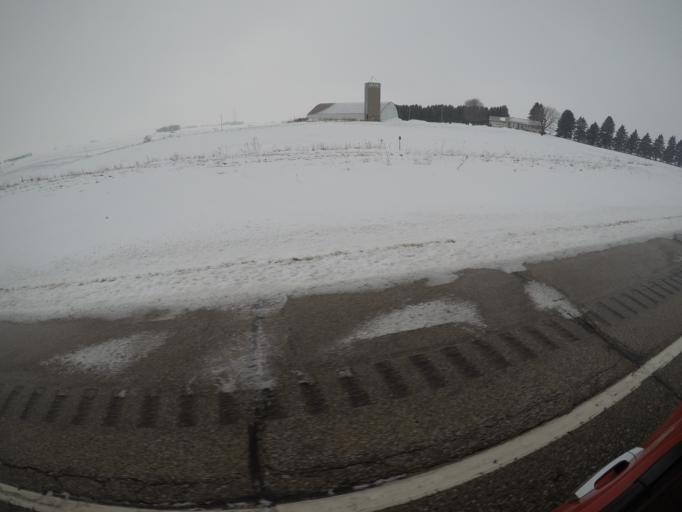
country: US
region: Minnesota
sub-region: Goodhue County
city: Wanamingo
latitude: 44.3789
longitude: -92.8159
